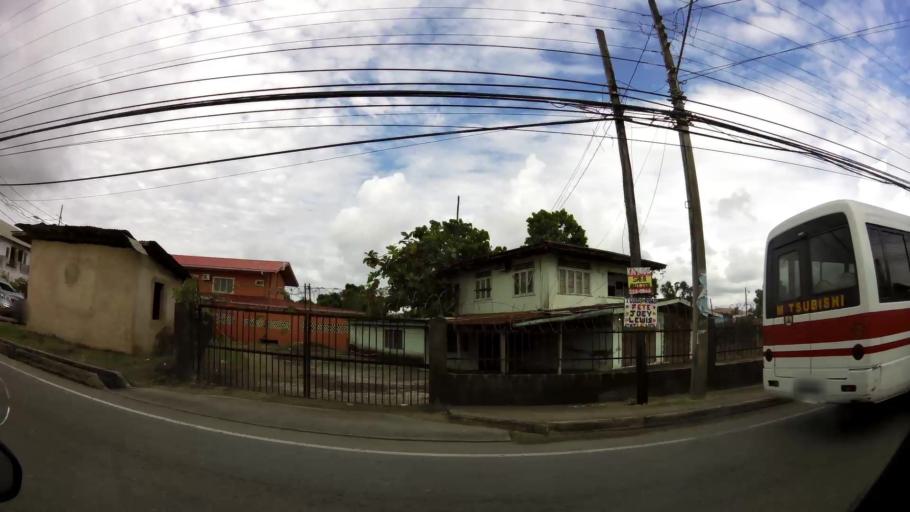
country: TT
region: Chaguanas
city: Chaguanas
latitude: 10.4800
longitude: -61.4093
